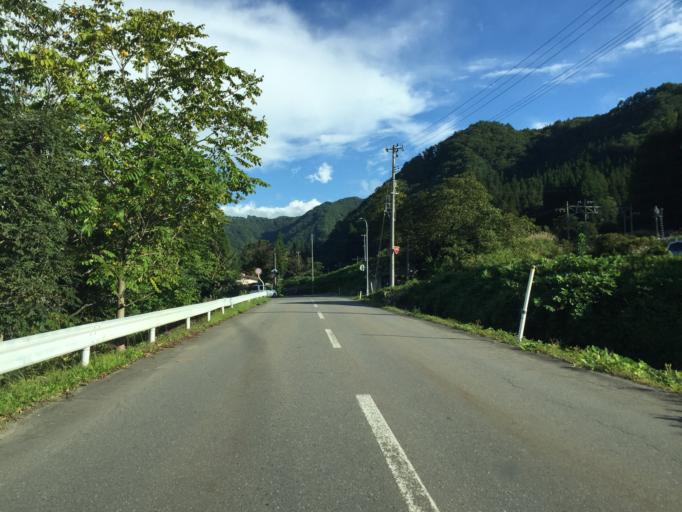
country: JP
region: Yamagata
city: Yonezawa
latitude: 37.8619
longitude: 140.1523
